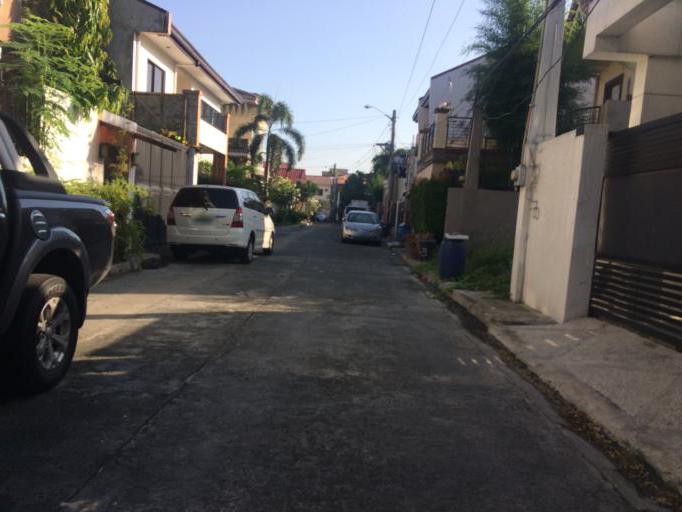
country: PH
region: Calabarzon
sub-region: Province of Rizal
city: Taytay
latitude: 14.5539
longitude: 121.1066
